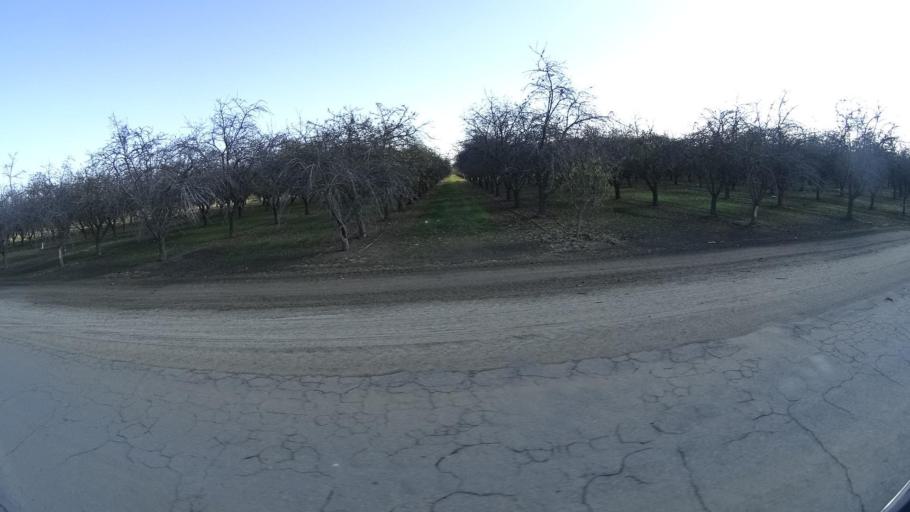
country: US
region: California
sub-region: Kern County
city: McFarland
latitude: 35.7119
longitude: -119.2586
